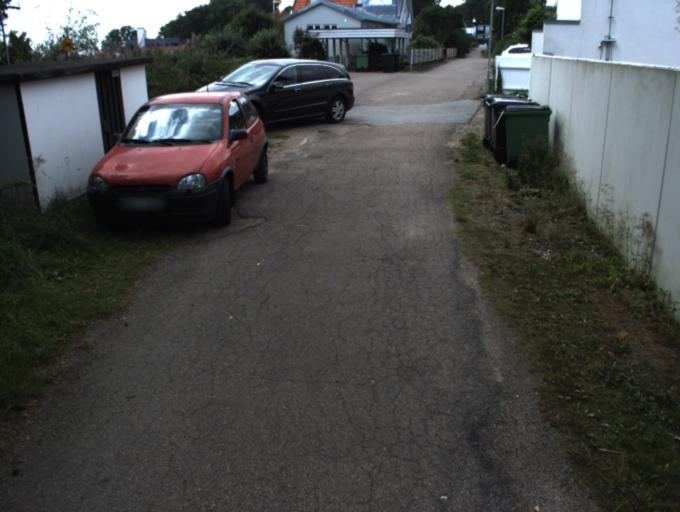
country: SE
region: Skane
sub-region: Helsingborg
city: Helsingborg
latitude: 56.0870
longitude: 12.6551
